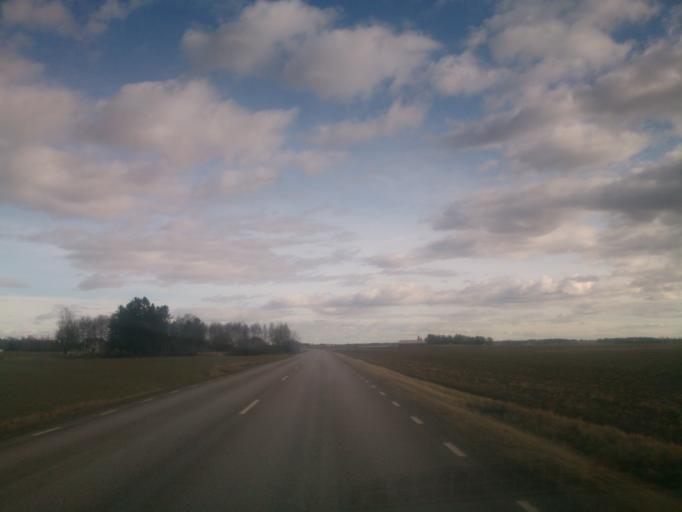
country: SE
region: OEstergoetland
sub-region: Motala Kommun
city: Borensberg
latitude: 58.4902
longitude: 15.3601
